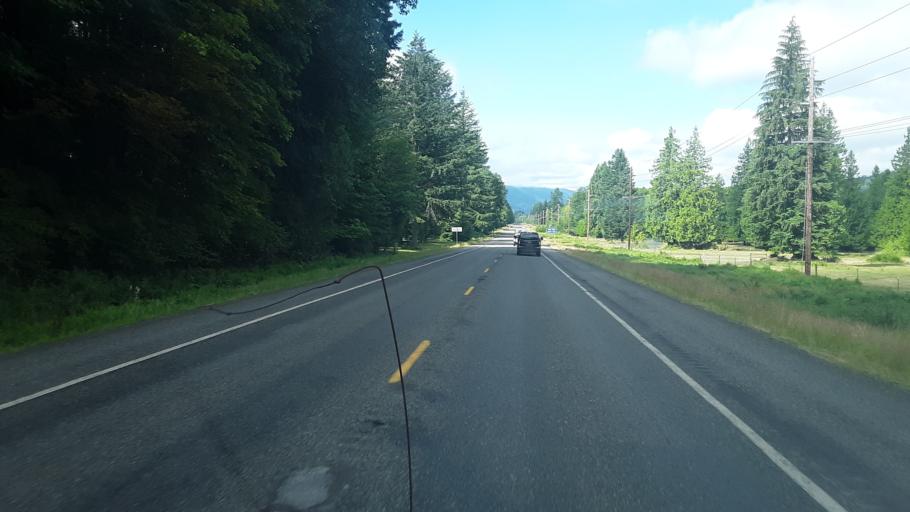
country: US
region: Washington
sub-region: Lewis County
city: Morton
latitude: 46.5626
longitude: -121.7165
